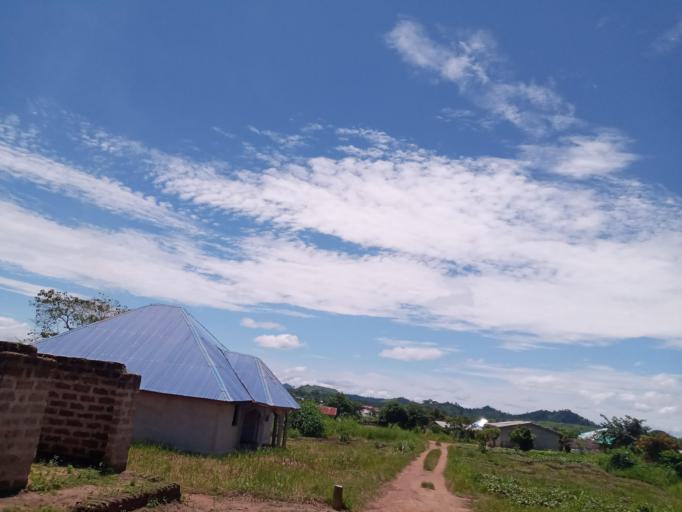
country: SL
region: Eastern Province
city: Koidu
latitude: 8.6345
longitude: -10.9407
